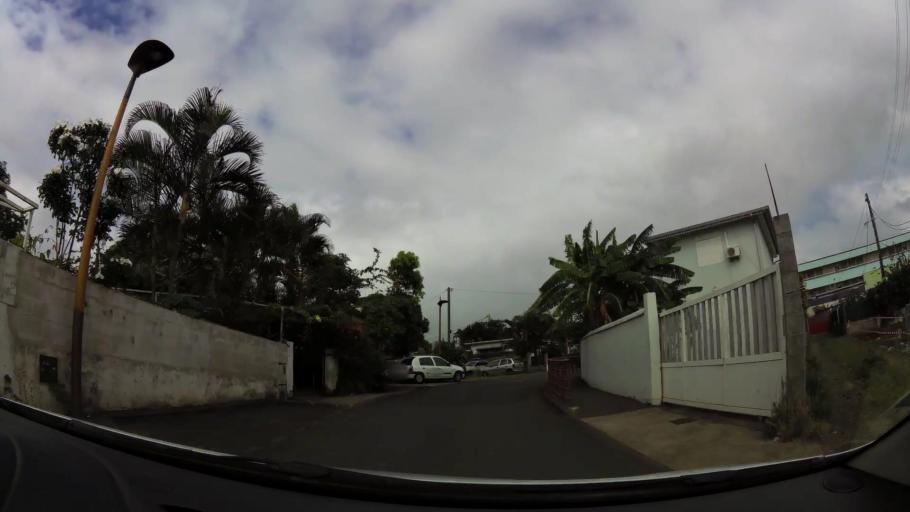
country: RE
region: Reunion
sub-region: Reunion
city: Sainte-Marie
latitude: -20.8949
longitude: 55.5551
